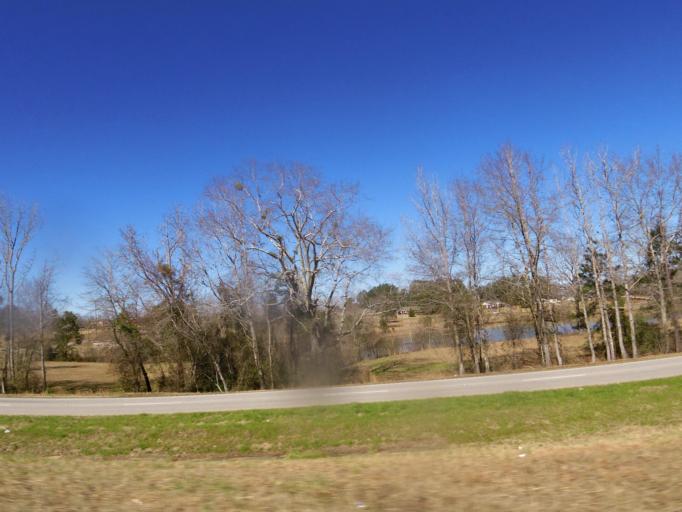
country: US
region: Alabama
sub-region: Bullock County
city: Union Springs
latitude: 32.1461
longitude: -85.6805
